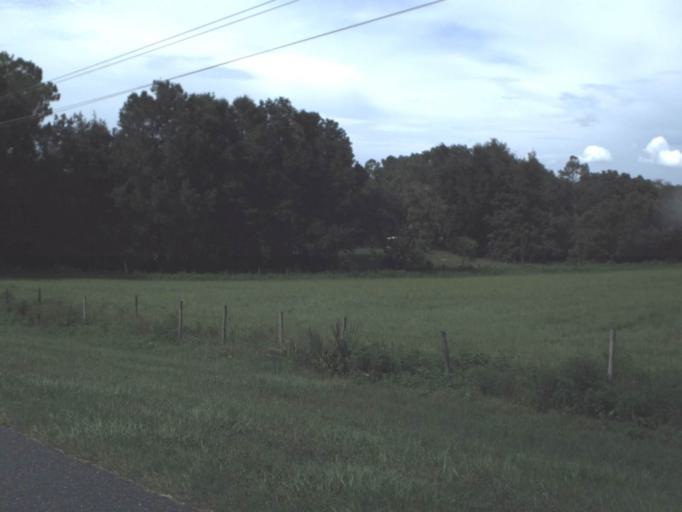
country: US
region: Florida
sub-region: Gilchrist County
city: Trenton
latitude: 29.8085
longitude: -82.8670
